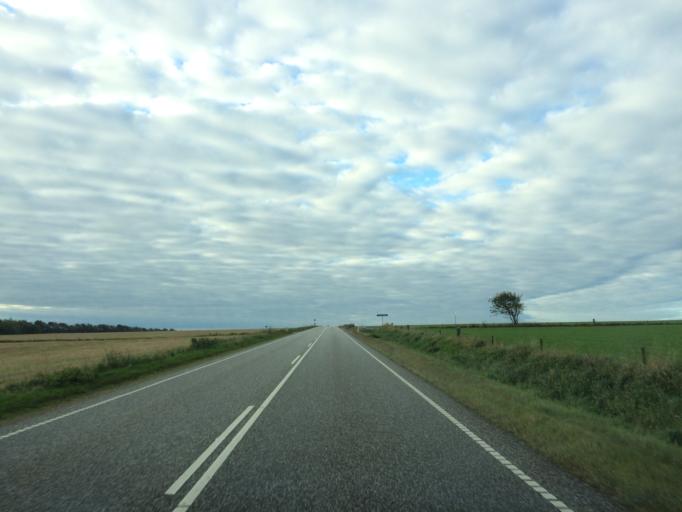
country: DK
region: Central Jutland
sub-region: Ringkobing-Skjern Kommune
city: Skjern
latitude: 56.0530
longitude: 8.5039
